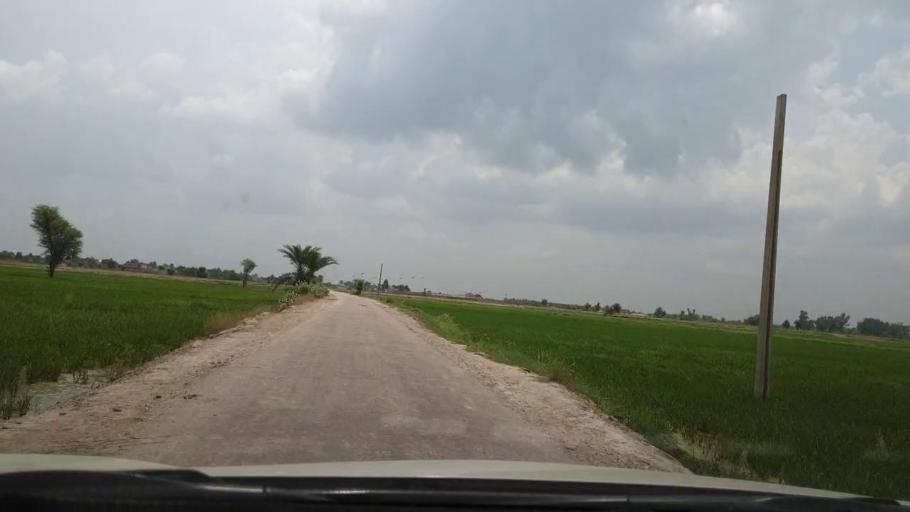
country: PK
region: Sindh
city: Goth Garelo
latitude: 27.4264
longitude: 68.1075
